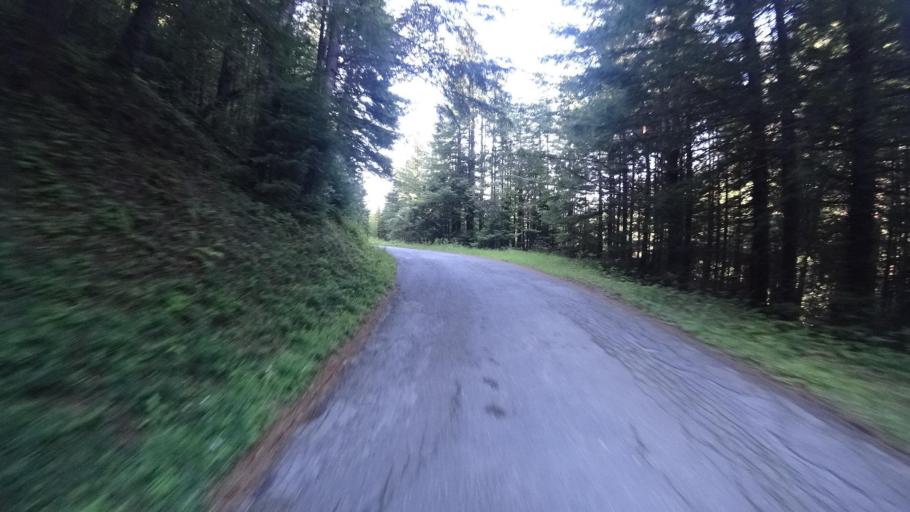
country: US
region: California
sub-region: Humboldt County
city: Rio Dell
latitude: 40.4595
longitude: -123.9953
